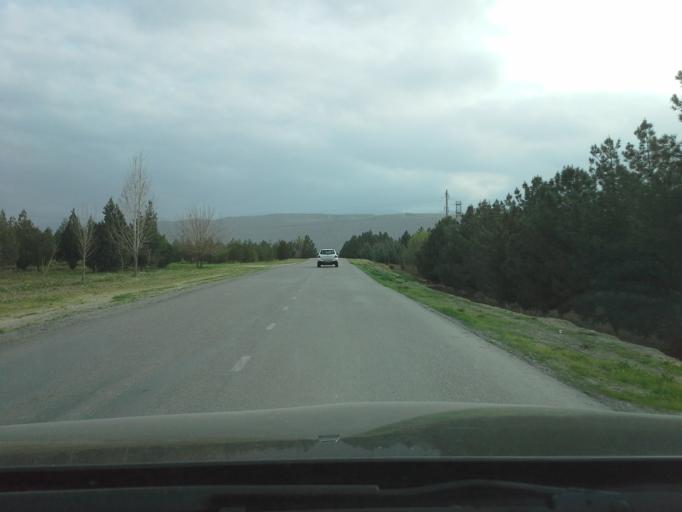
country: TM
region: Ahal
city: Abadan
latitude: 37.9514
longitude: 58.2275
